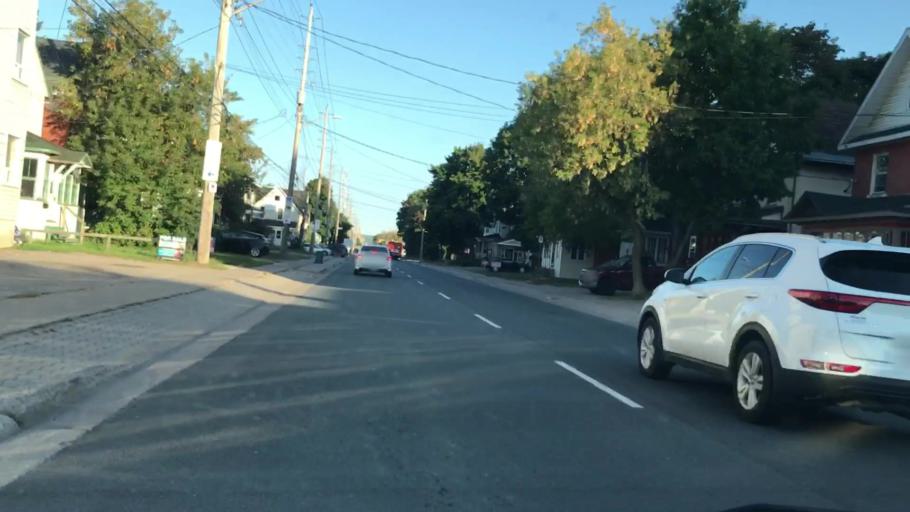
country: CA
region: Ontario
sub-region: Algoma
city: Sault Ste. Marie
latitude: 46.5132
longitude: -84.3302
